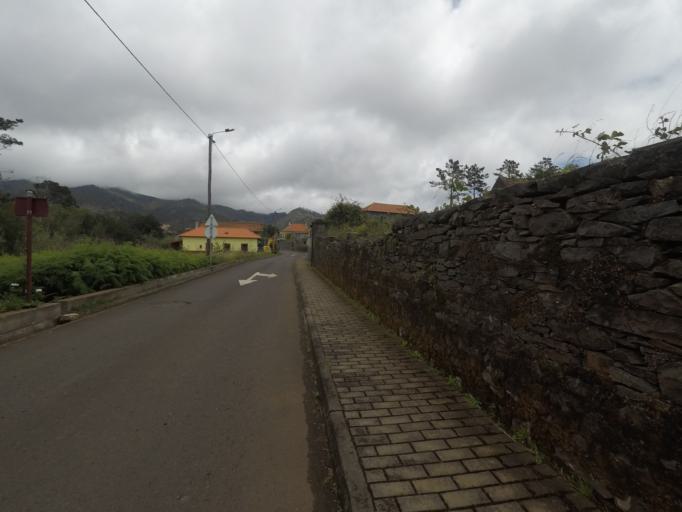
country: PT
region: Madeira
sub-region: Calheta
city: Estreito da Calheta
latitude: 32.7533
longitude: -17.2055
